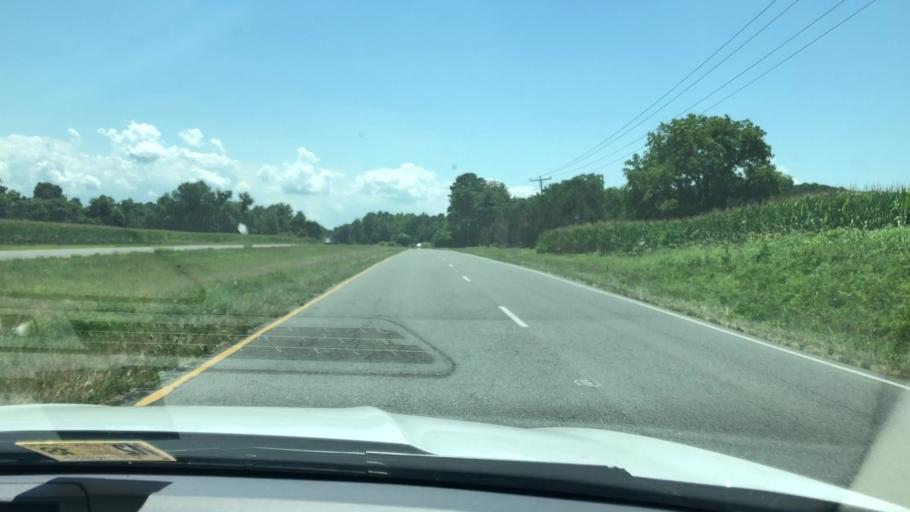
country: US
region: Virginia
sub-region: Lancaster County
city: Kilmarnock
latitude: 37.6712
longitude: -76.3796
